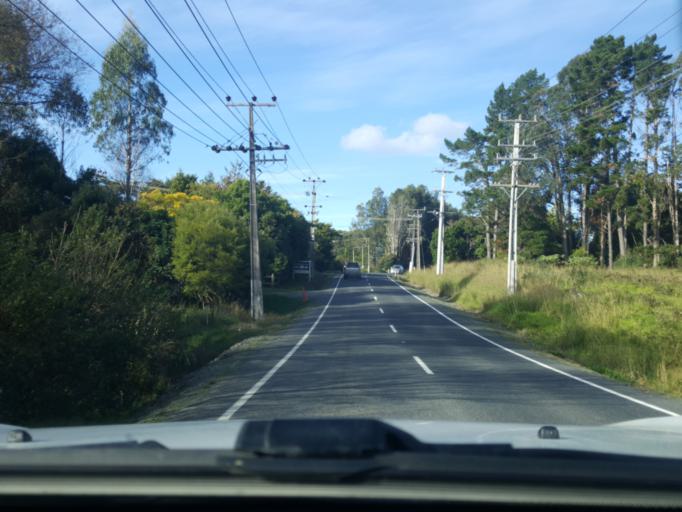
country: NZ
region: Auckland
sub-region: Auckland
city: Muriwai Beach
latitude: -36.7618
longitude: 174.5810
